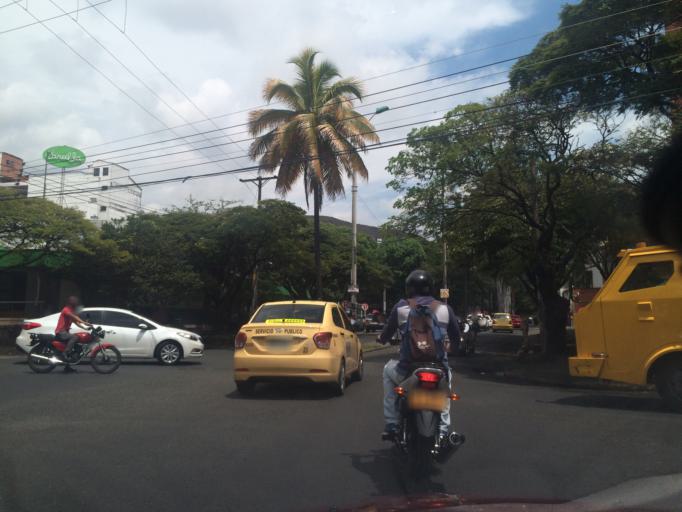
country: CO
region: Valle del Cauca
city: Cali
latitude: 3.4335
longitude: -76.5437
